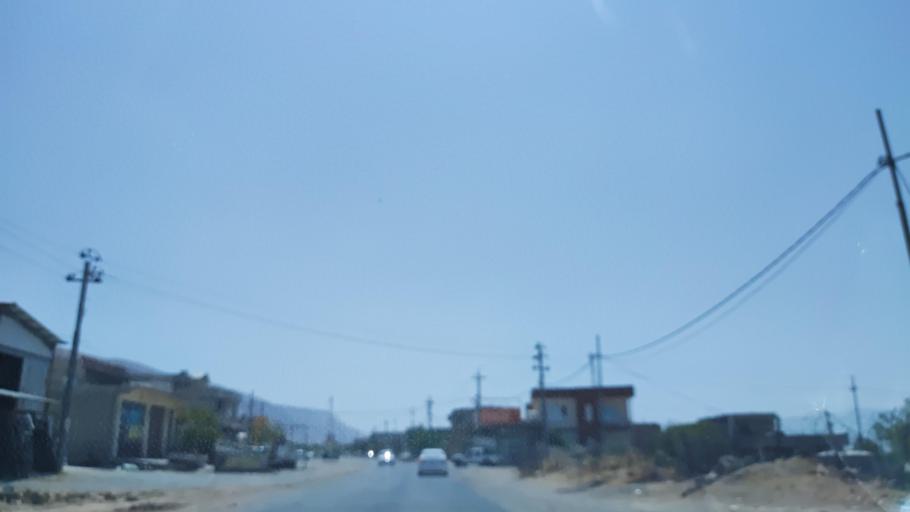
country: IQ
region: Arbil
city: Shaqlawah
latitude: 36.5699
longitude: 44.3341
